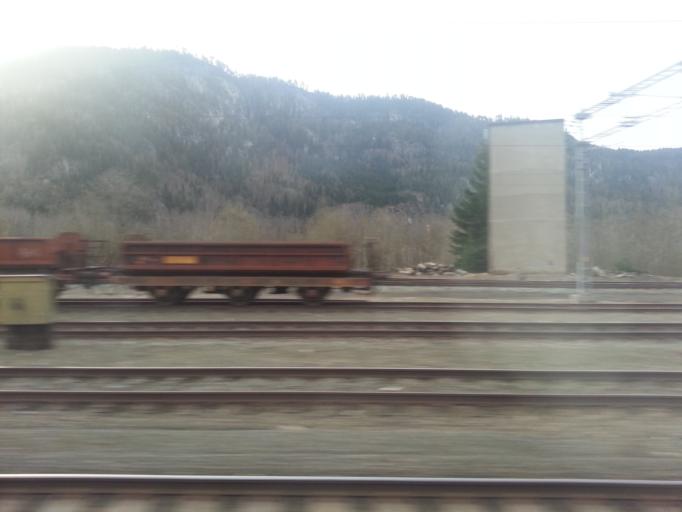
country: NO
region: Sor-Trondelag
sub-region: Midtre Gauldal
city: Storen
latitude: 63.0533
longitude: 10.2852
